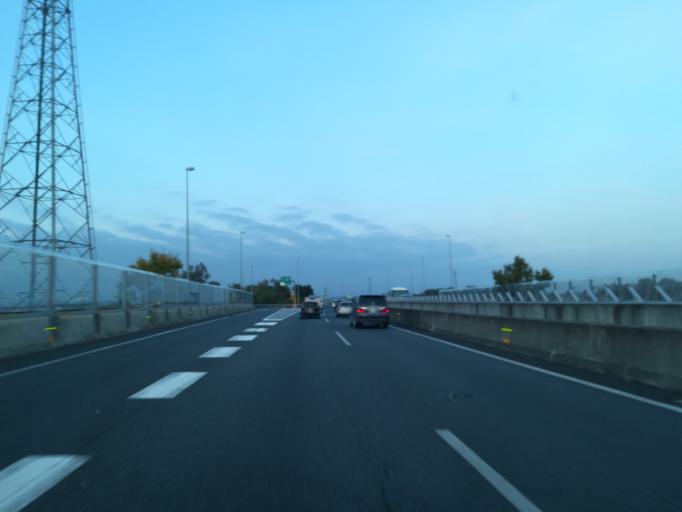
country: JP
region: Gunma
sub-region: Sawa-gun
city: Tamamura
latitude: 36.3460
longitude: 139.1408
